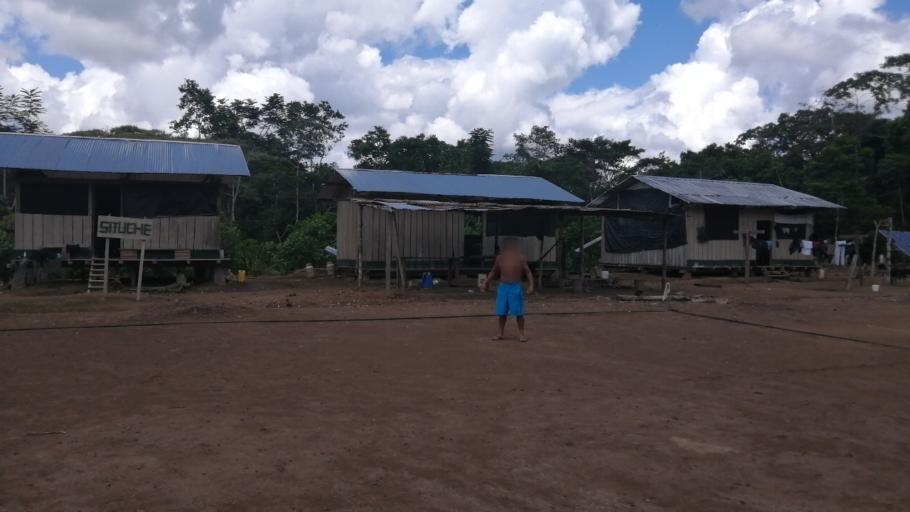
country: EC
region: Morona-Santiago
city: Taisha
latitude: -2.8087
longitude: -77.3023
